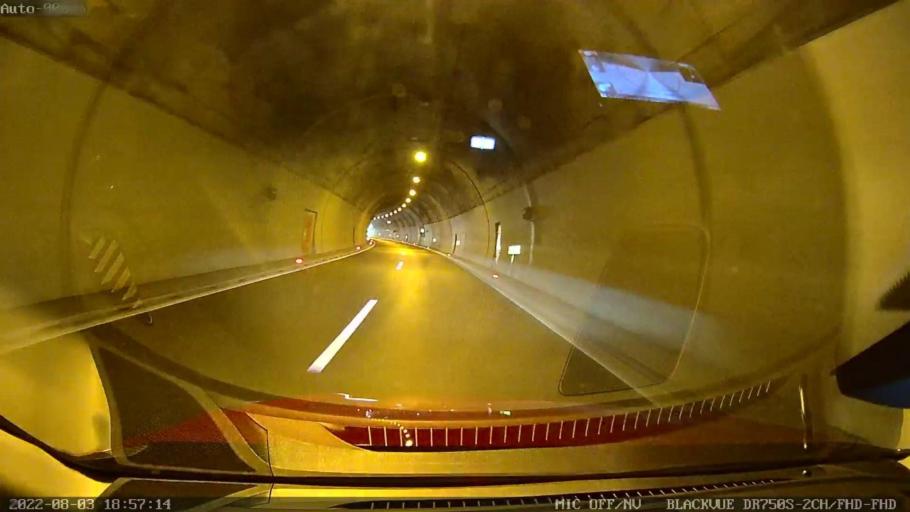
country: SI
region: Vipava
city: Vipava
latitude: 45.8001
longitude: 13.9812
